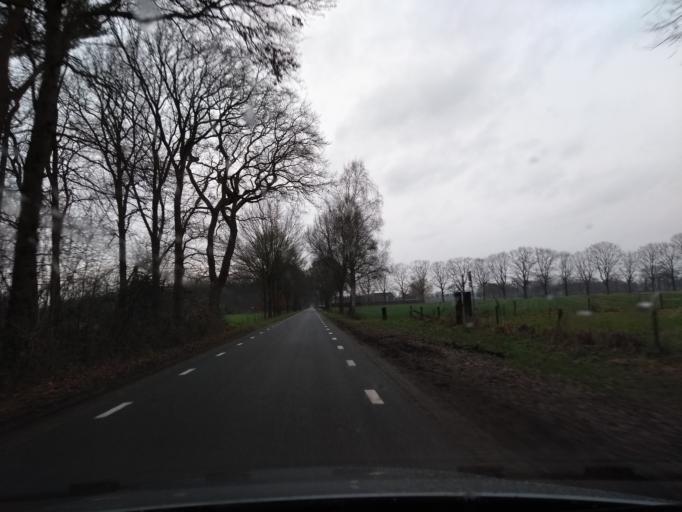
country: NL
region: Gelderland
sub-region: Gemeente Bronckhorst
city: Zelhem
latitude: 52.0351
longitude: 6.3425
